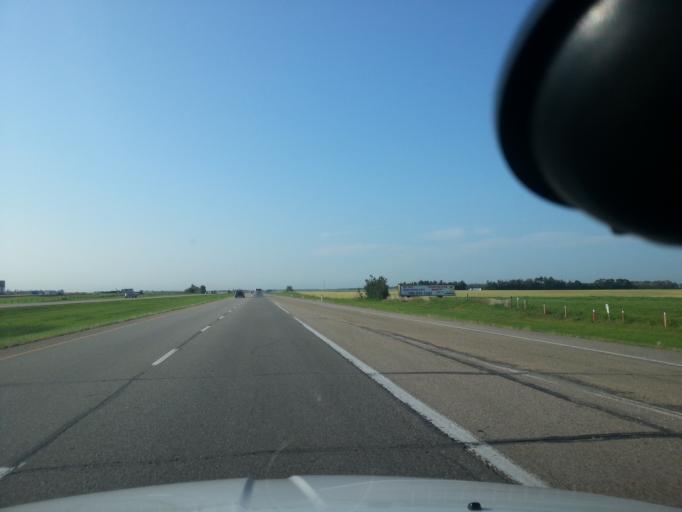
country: CA
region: Alberta
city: Leduc
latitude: 53.1899
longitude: -113.5984
